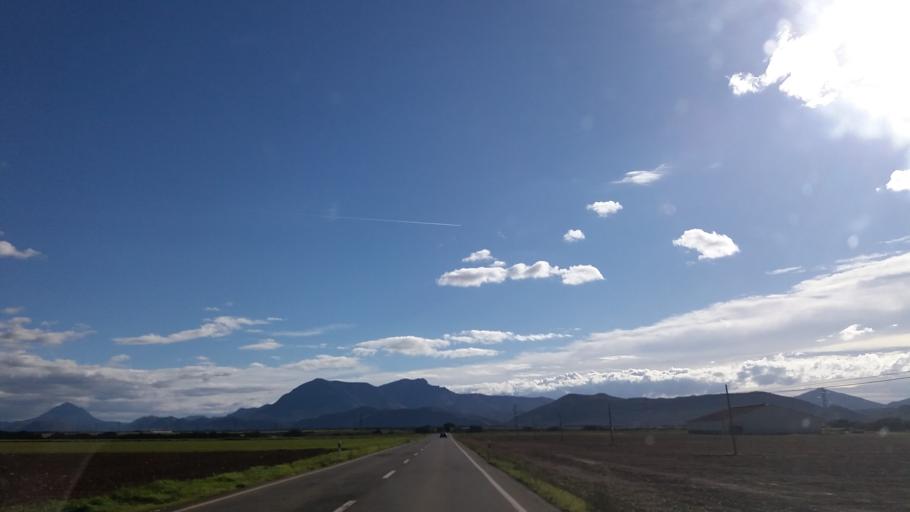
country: ES
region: Aragon
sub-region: Provincia de Huesca
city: Bailo
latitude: 42.5934
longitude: -0.8443
